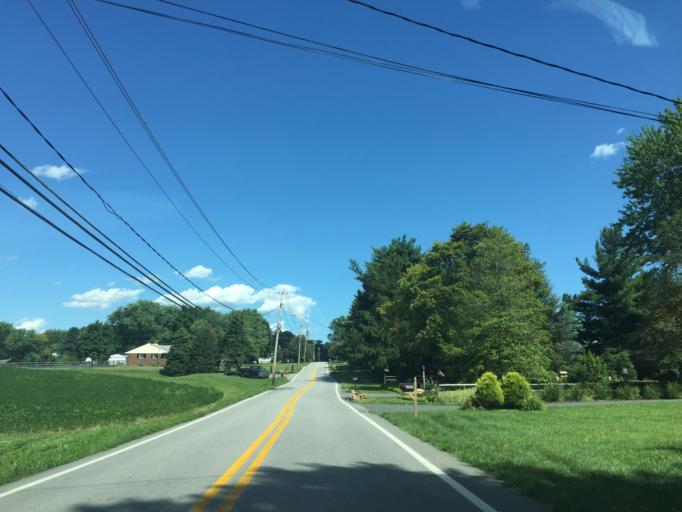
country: US
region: Maryland
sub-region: Baltimore County
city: Perry Hall
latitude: 39.4120
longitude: -76.4742
